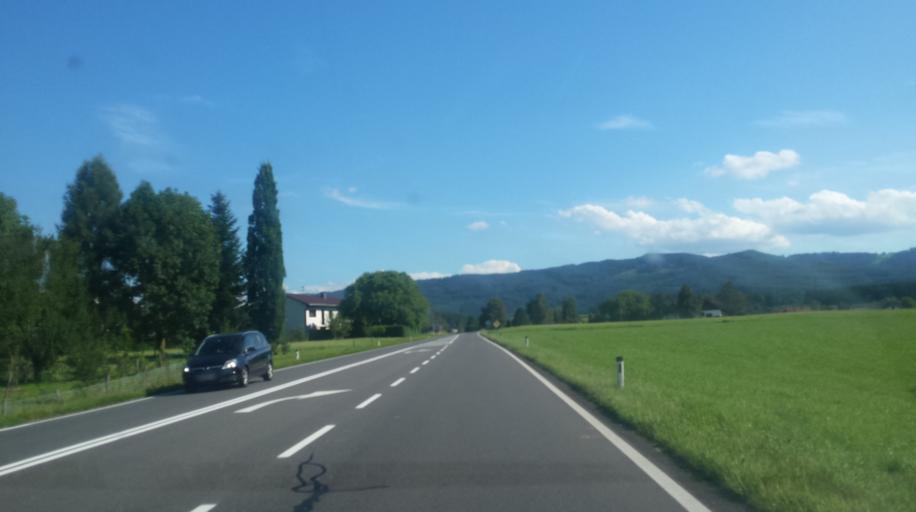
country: AT
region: Upper Austria
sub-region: Politischer Bezirk Vocklabruck
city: Attnang-Puchheim
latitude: 47.9755
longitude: 13.7023
